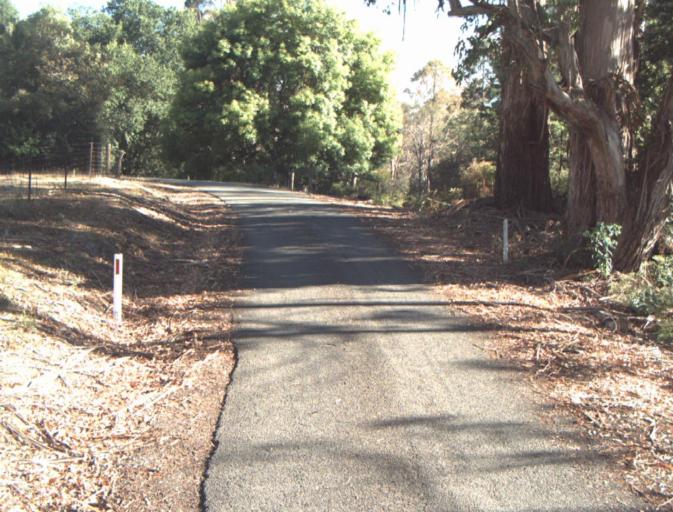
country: AU
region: Tasmania
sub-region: Launceston
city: Mayfield
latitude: -41.3010
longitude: 147.1986
